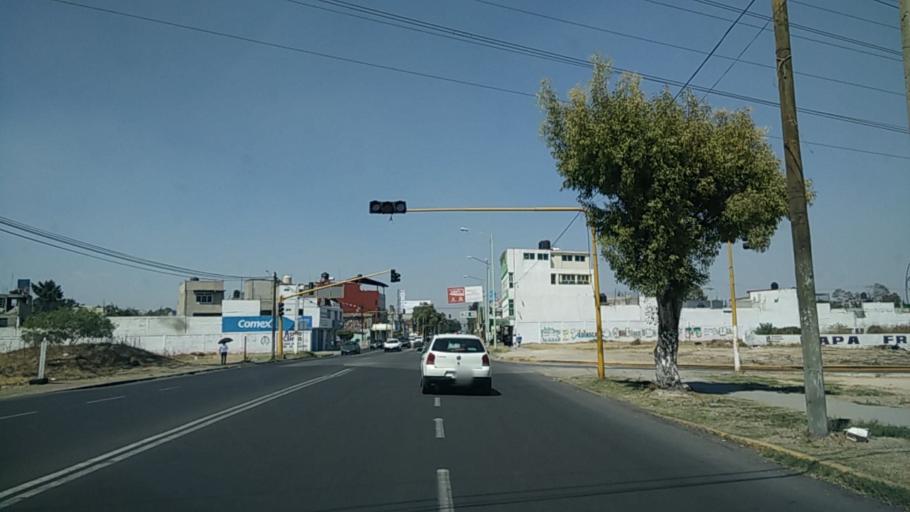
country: MX
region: Mexico
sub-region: Atenco
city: Colonia el Salado
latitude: 19.5893
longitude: -99.0267
